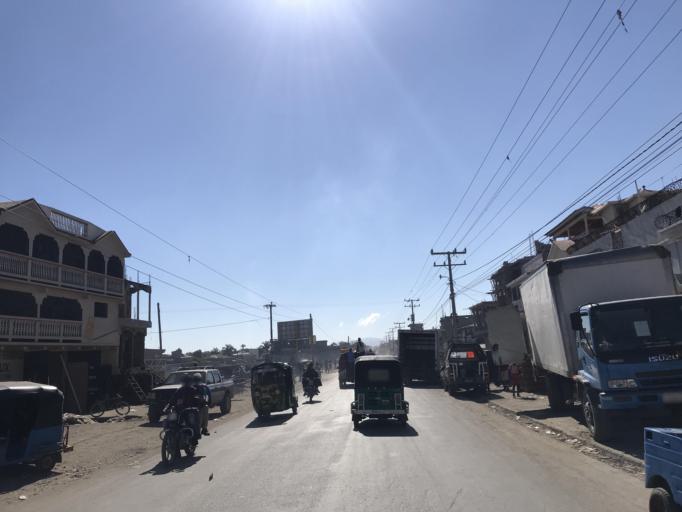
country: HT
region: Nord
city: Okap
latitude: 19.7349
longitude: -72.1869
